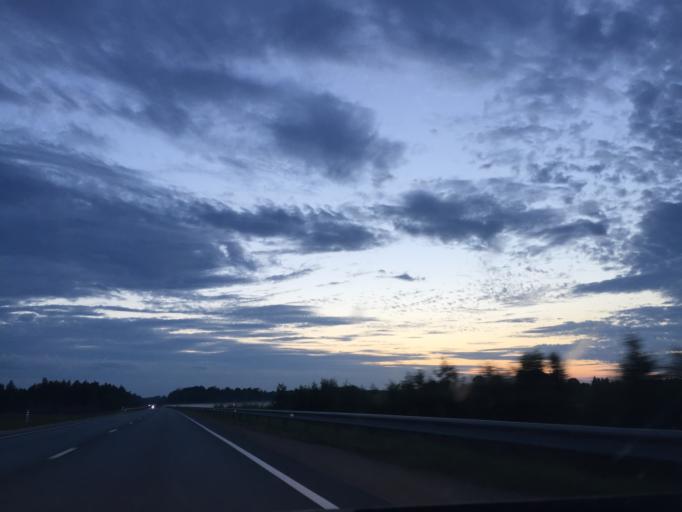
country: LV
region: Ogre
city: Jumprava
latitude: 56.7945
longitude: 24.9737
